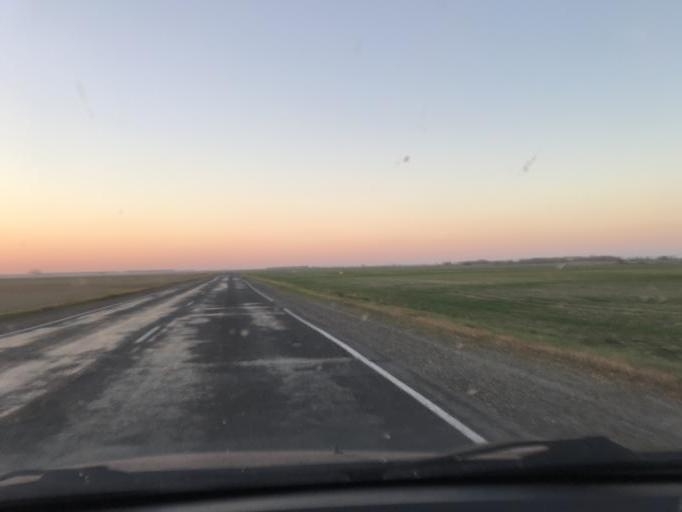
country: BY
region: Gomel
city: Horad Rechytsa
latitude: 52.1622
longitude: 30.5856
